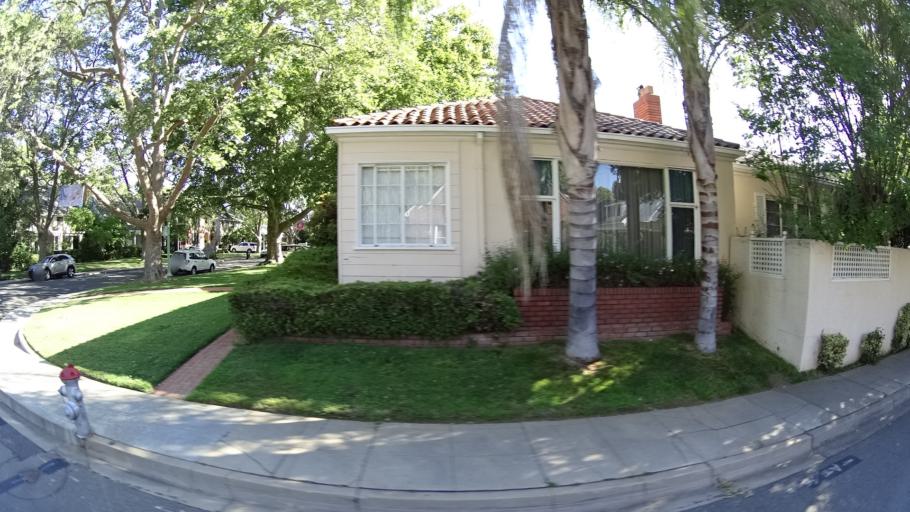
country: US
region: California
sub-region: Sacramento County
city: Sacramento
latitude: 38.5664
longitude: -121.4525
